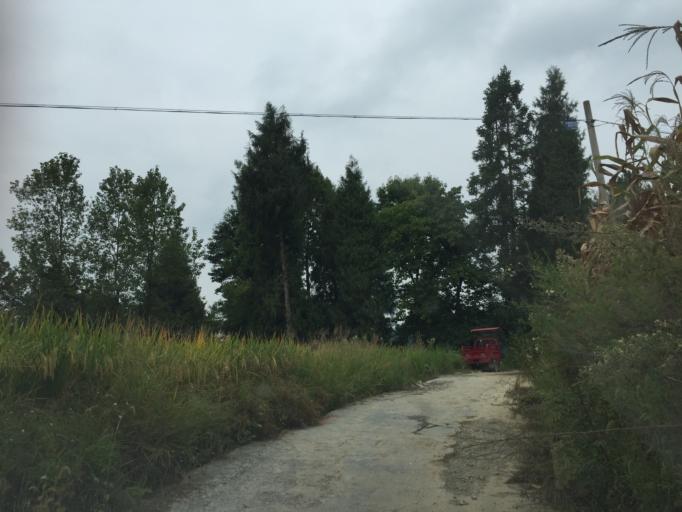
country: CN
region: Guizhou Sheng
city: Longquan
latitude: 28.2087
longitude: 108.0371
